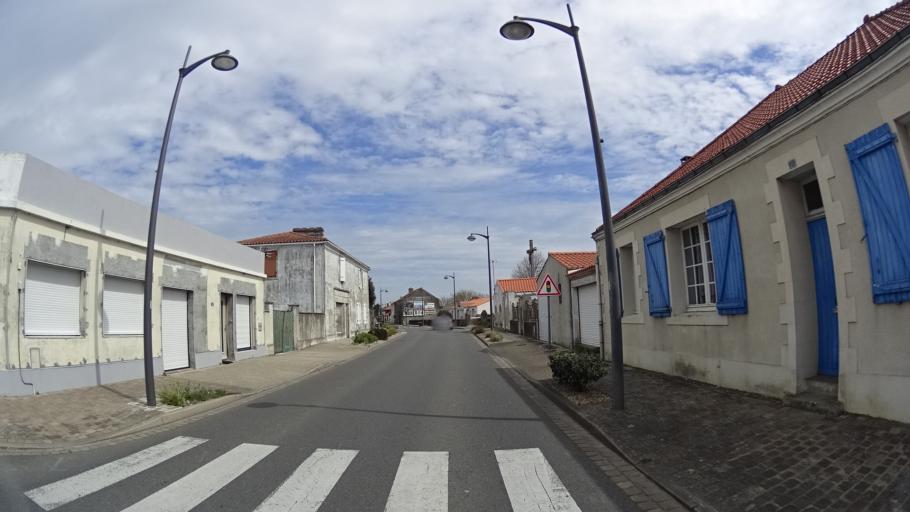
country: FR
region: Pays de la Loire
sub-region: Departement de la Vendee
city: Bouin
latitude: 46.9719
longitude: -1.9982
